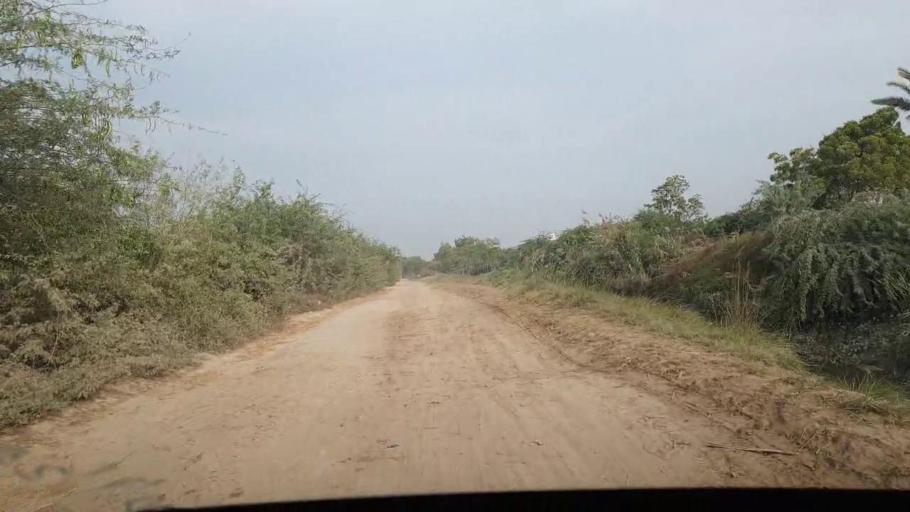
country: PK
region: Sindh
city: Chuhar Jamali
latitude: 24.3943
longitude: 67.9738
